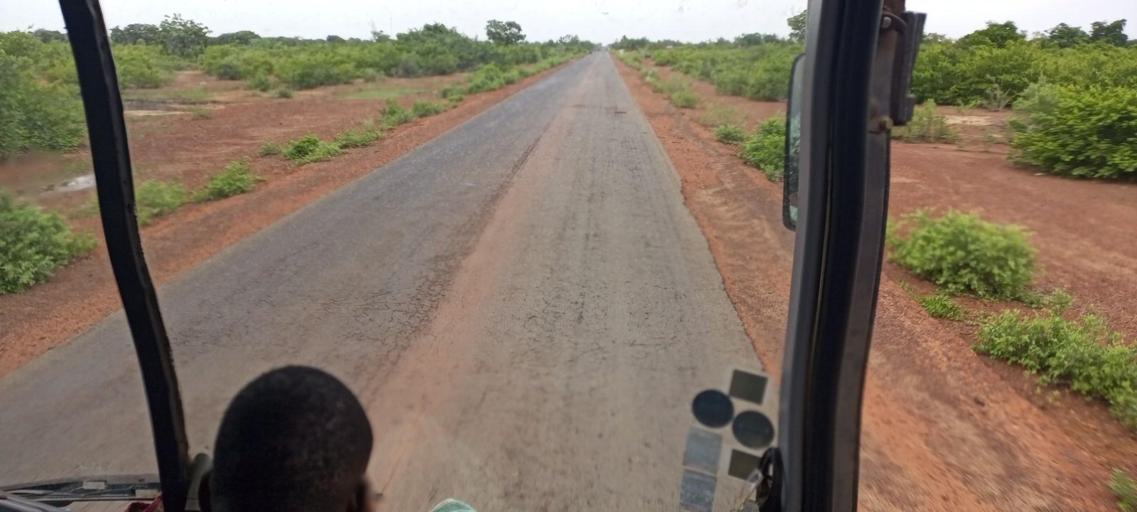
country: ML
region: Sikasso
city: Koutiala
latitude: 12.5497
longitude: -5.5835
